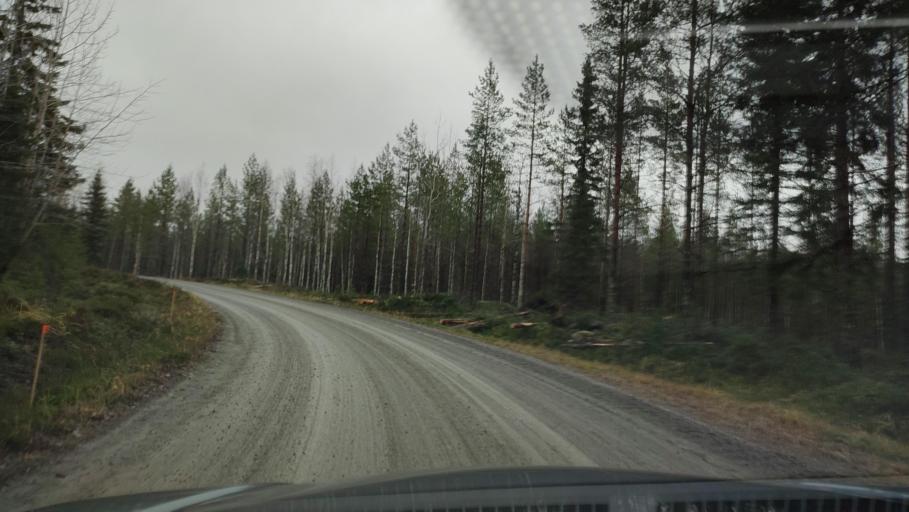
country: FI
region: Southern Ostrobothnia
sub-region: Suupohja
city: Karijoki
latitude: 62.1291
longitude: 21.6163
